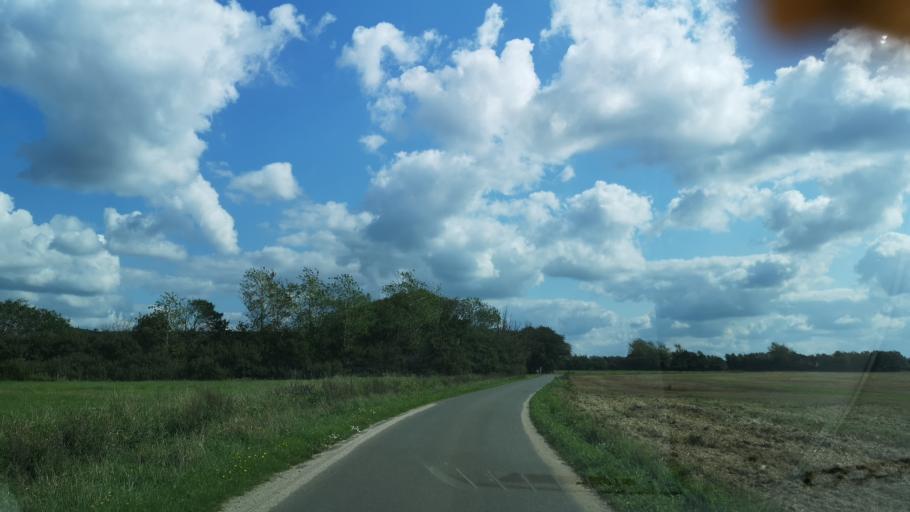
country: DK
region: Central Jutland
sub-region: Ringkobing-Skjern Kommune
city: Skjern
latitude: 55.8956
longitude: 8.3956
